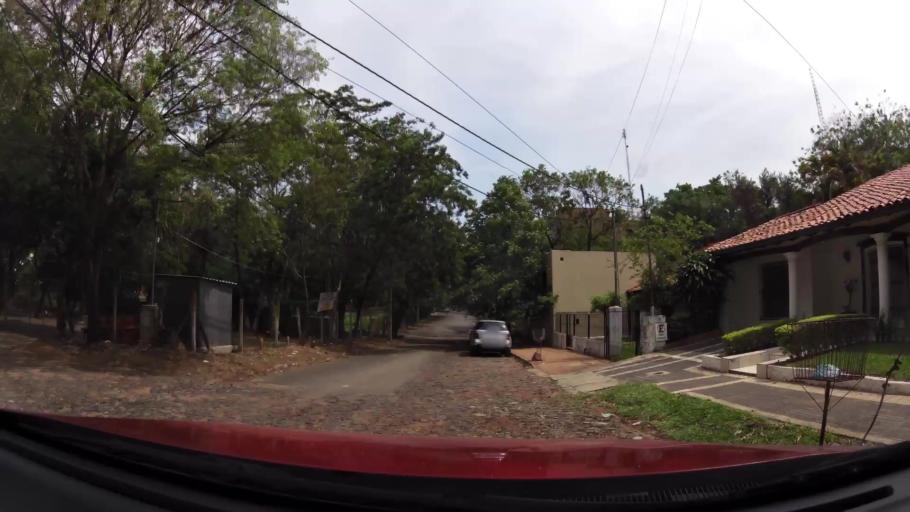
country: PY
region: Asuncion
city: Asuncion
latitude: -25.2918
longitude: -57.5818
